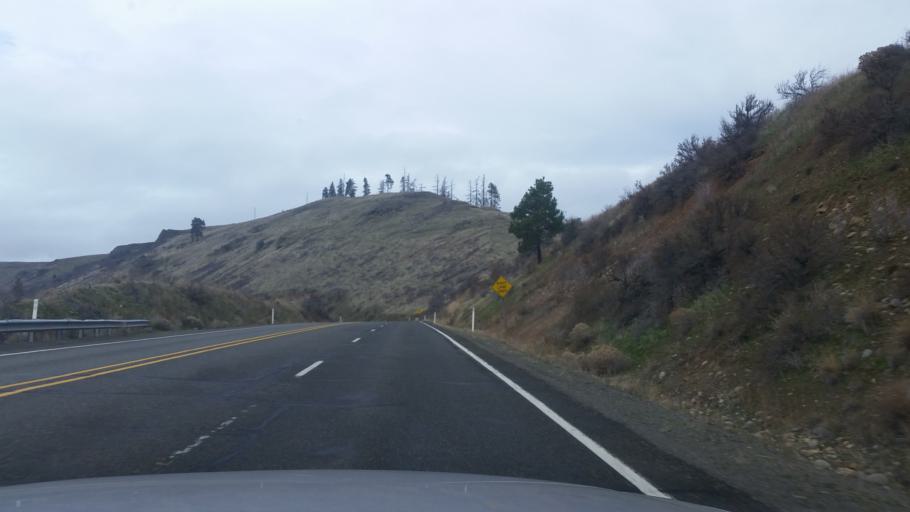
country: US
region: Washington
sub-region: Kittitas County
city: Cle Elum
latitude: 47.1272
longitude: -120.7465
